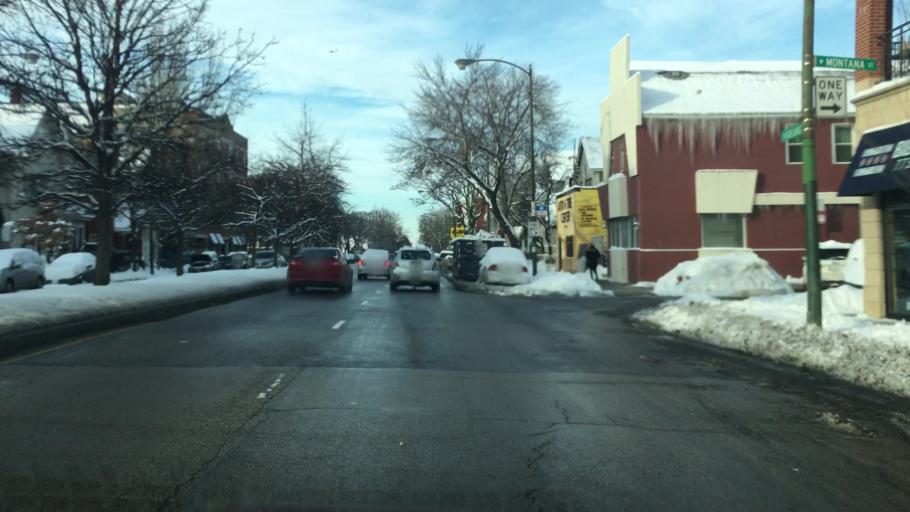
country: US
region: Illinois
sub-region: Cook County
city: Chicago
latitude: 41.9259
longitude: -87.6681
